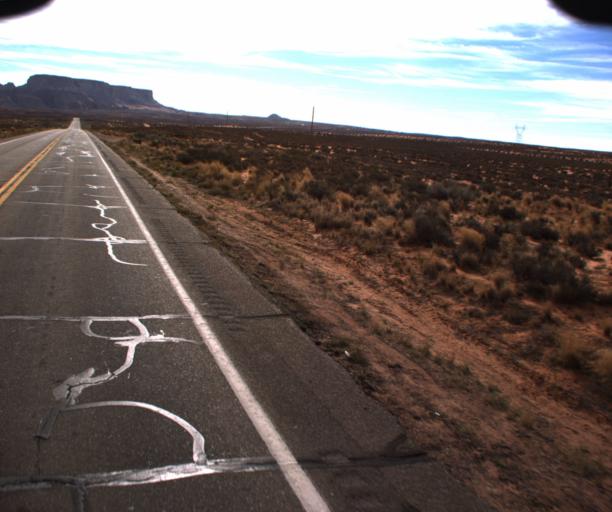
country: US
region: Arizona
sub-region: Coconino County
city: LeChee
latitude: 36.8855
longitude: -111.3590
